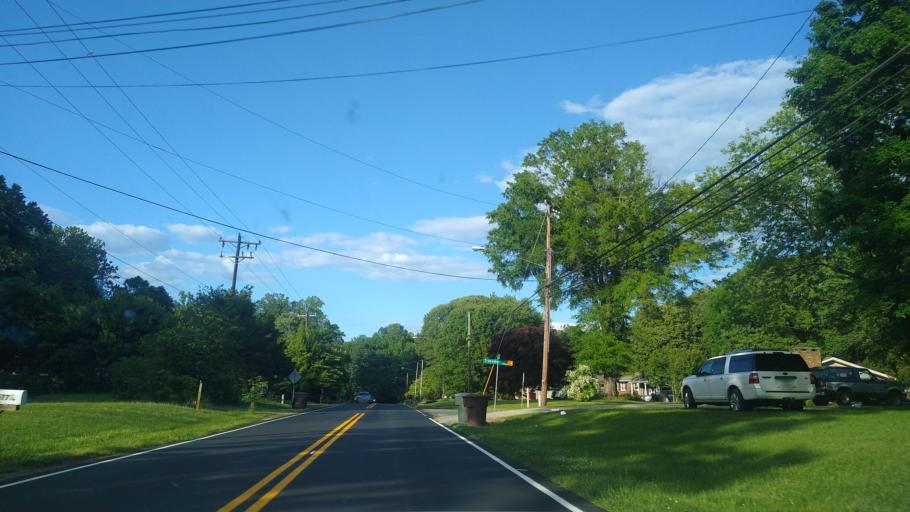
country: US
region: North Carolina
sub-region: Guilford County
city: McLeansville
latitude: 36.1684
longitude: -79.7273
